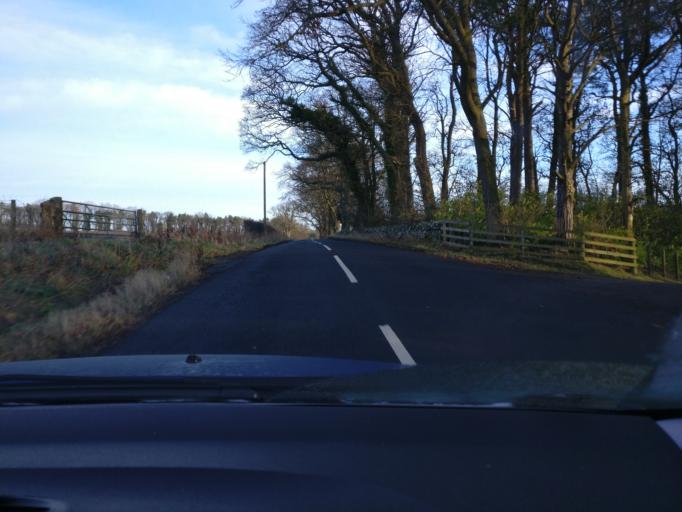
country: GB
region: Scotland
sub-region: The Scottish Borders
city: Hawick
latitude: 55.4415
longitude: -2.7706
